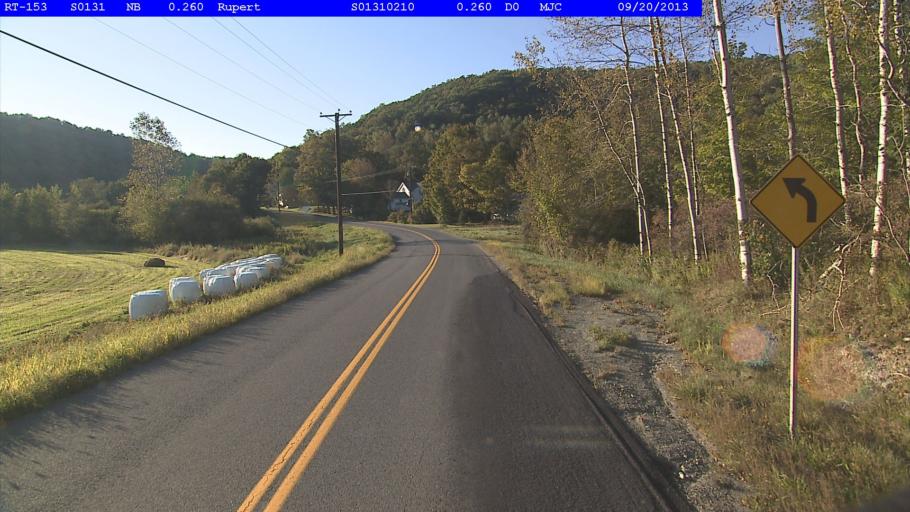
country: US
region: New York
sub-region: Washington County
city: Granville
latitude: 43.2625
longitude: -73.2265
